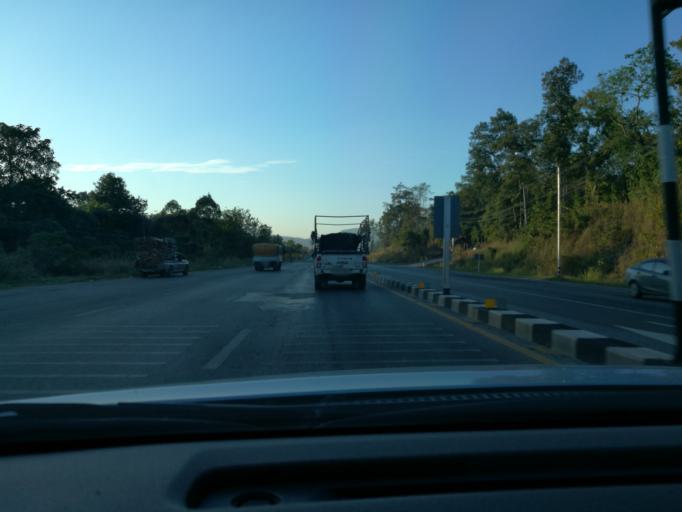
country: TH
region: Phitsanulok
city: Wang Thong
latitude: 16.8487
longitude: 100.5196
